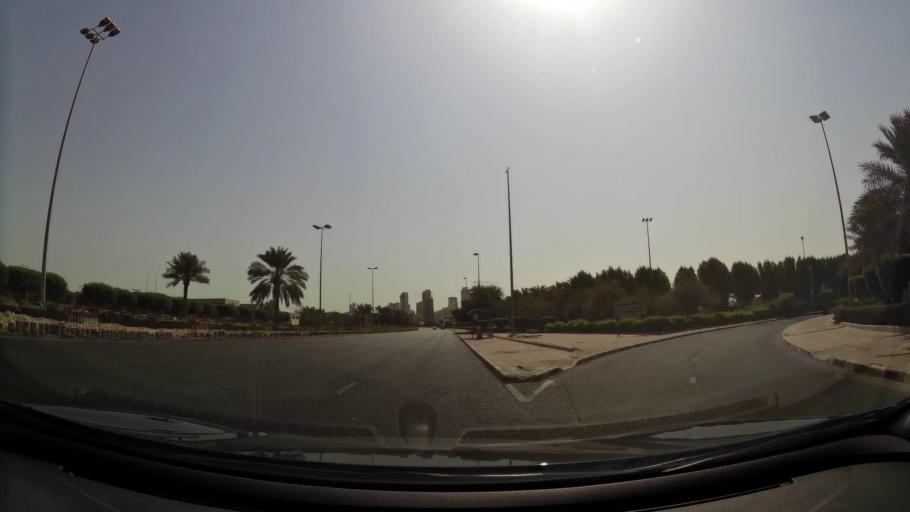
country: KW
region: Al Asimah
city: Ad Dasmah
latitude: 29.3649
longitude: 48.0220
